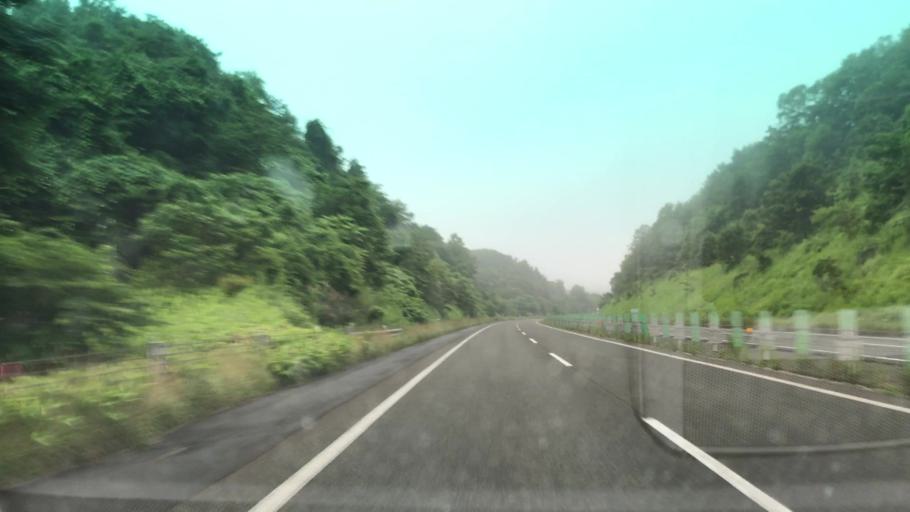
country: JP
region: Hokkaido
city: Shiraoi
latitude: 42.4903
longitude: 141.2373
